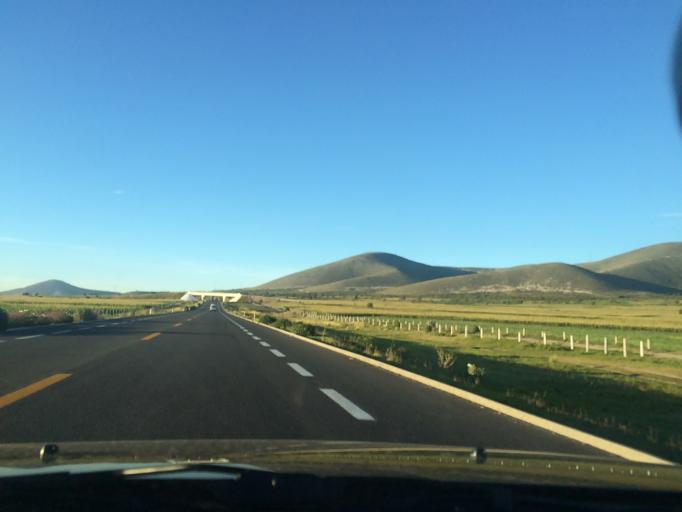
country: MX
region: Puebla
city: Morelos Canada
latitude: 18.7458
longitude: -97.4788
